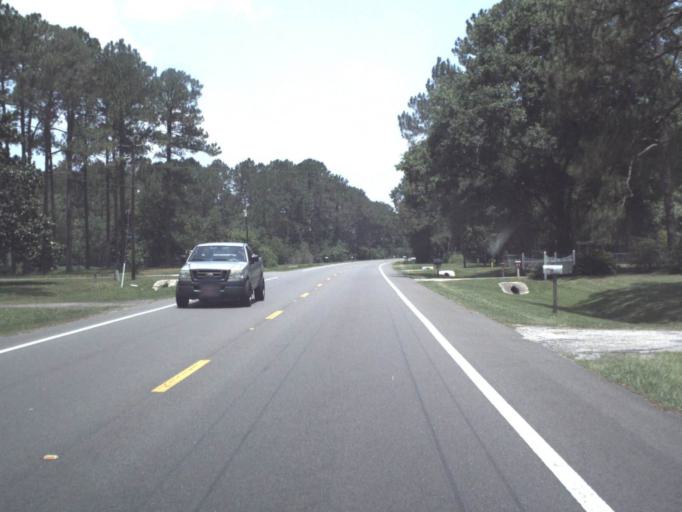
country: US
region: Florida
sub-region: Nassau County
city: Nassau Village-Ratliff
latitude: 30.5326
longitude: -81.7726
